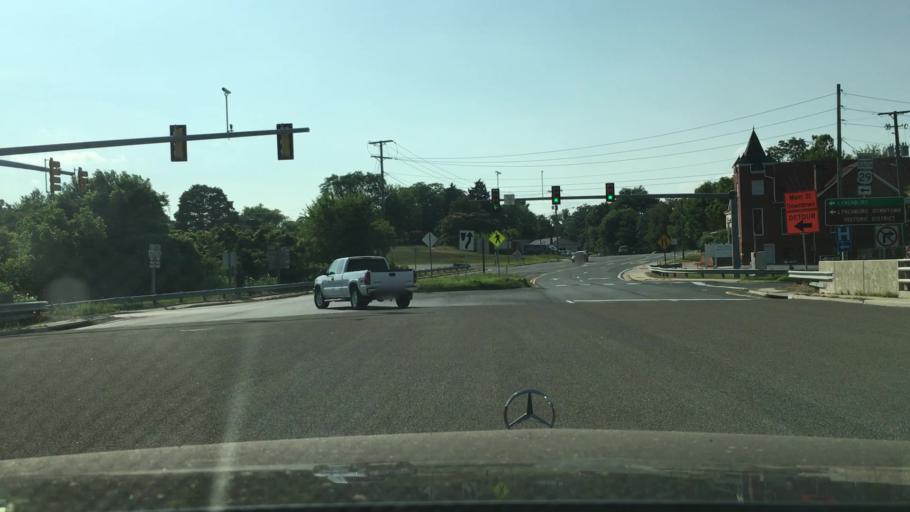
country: US
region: Virginia
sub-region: Amherst County
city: Madison Heights
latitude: 37.4221
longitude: -79.1228
